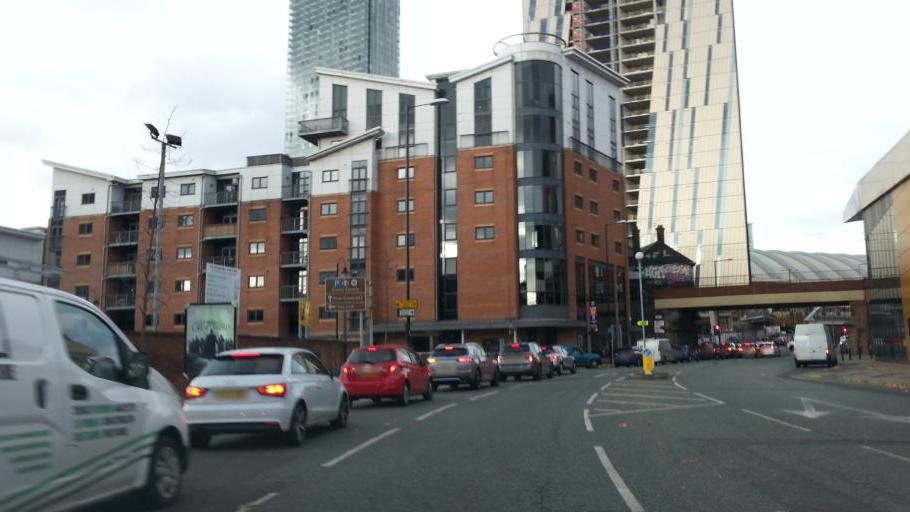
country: GB
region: England
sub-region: Manchester
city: Hulme
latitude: 53.4732
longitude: -2.2482
